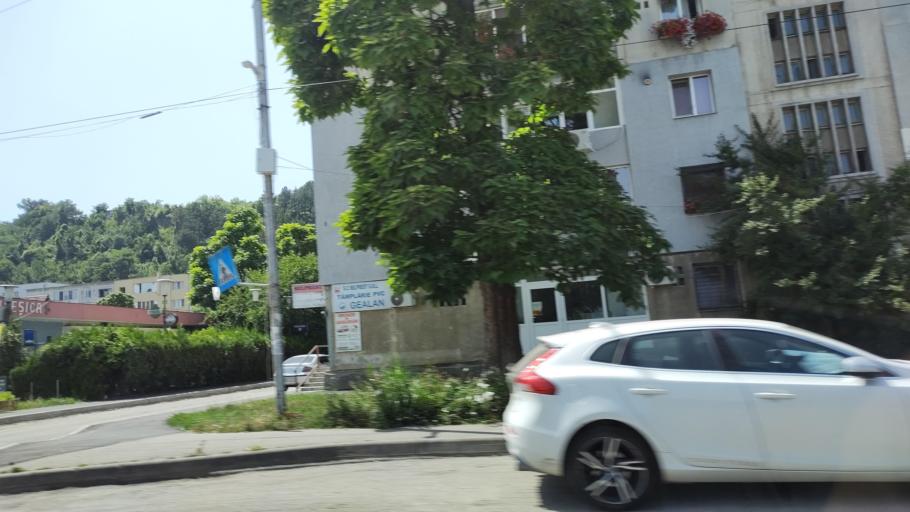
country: RO
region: Mehedinti
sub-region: Municipiul Orsova
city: Orsova
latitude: 44.7301
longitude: 22.4020
